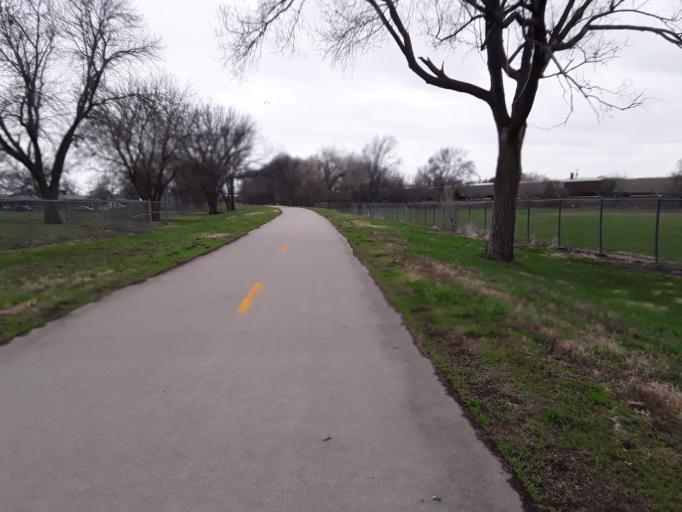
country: US
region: Nebraska
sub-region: Lancaster County
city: Lincoln
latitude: 40.8514
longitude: -96.6505
